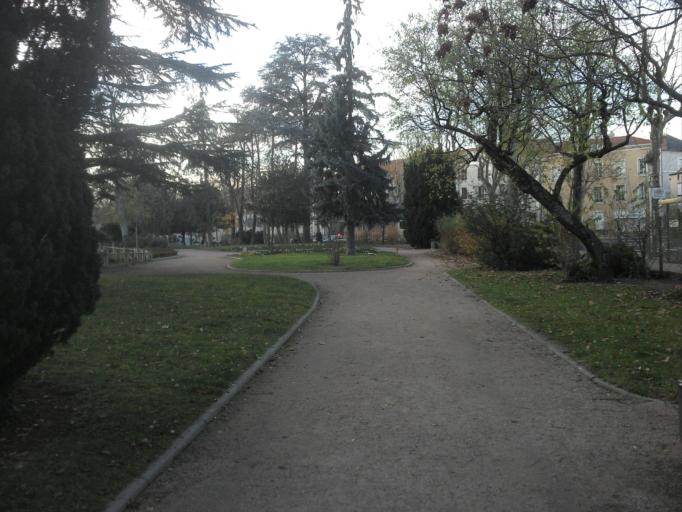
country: FR
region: Auvergne
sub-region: Departement du Puy-de-Dome
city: Riom
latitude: 45.8907
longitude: 3.1161
